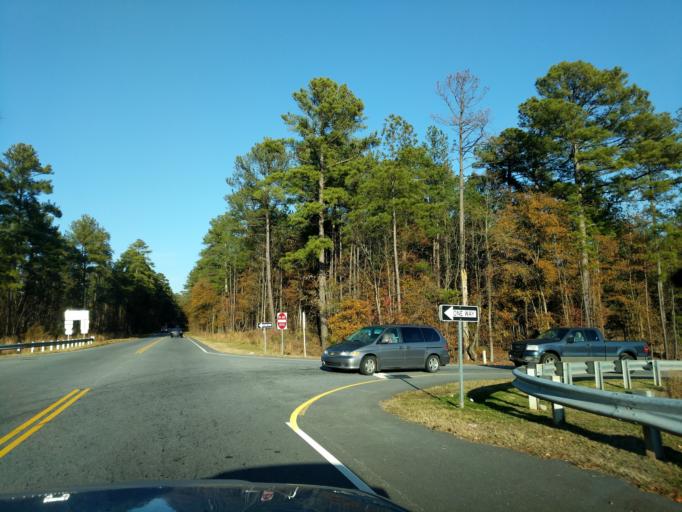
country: US
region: South Carolina
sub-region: Spartanburg County
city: Saxon
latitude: 34.9778
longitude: -81.9501
